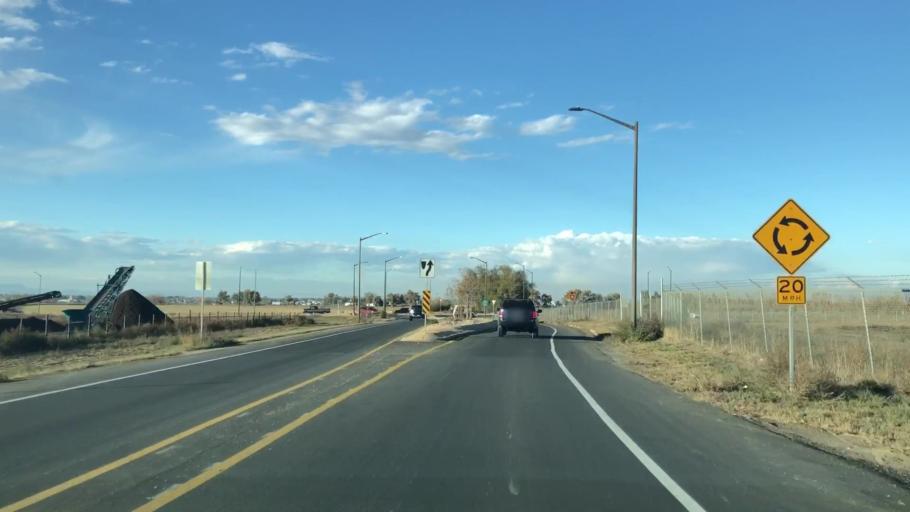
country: US
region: Colorado
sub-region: Larimer County
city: Loveland
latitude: 40.4641
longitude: -105.0203
